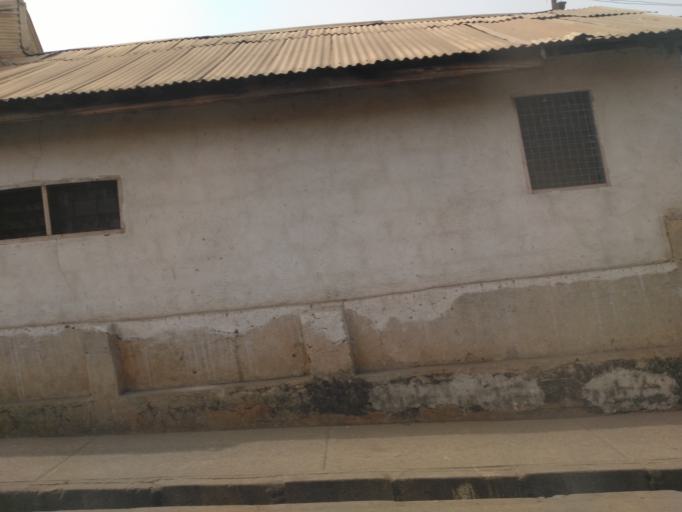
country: GH
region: Ashanti
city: Kumasi
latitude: 6.6978
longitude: -1.5961
